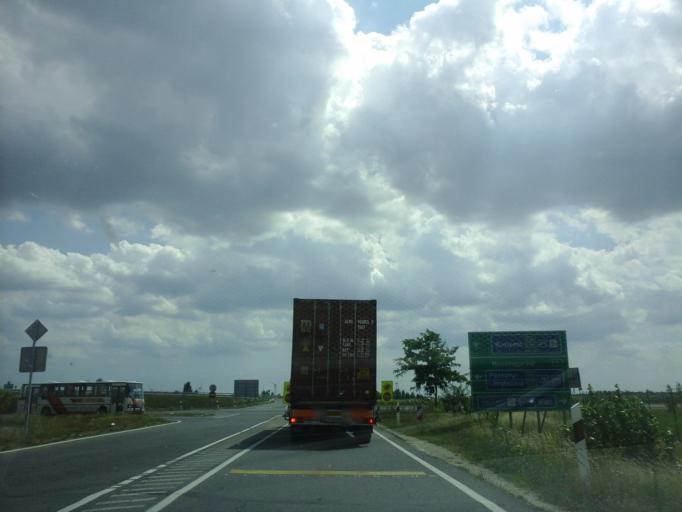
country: HU
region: Gyor-Moson-Sopron
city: Rajka
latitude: 47.9059
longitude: 17.1812
